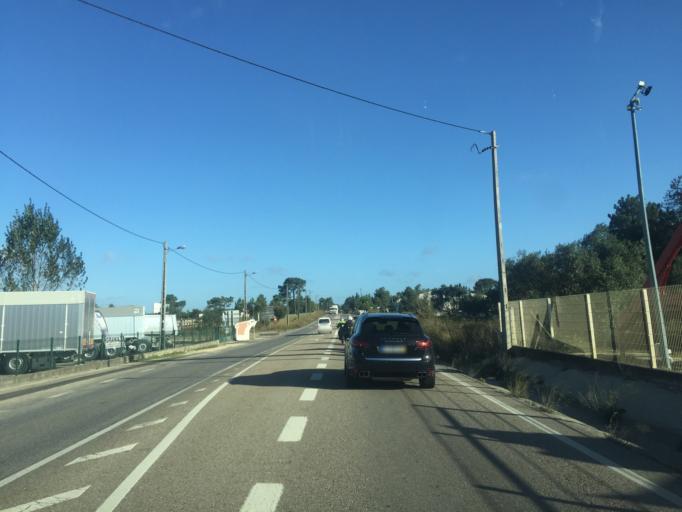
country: PT
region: Leiria
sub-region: Alcobaca
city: Benedita
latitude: 39.3828
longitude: -8.9616
